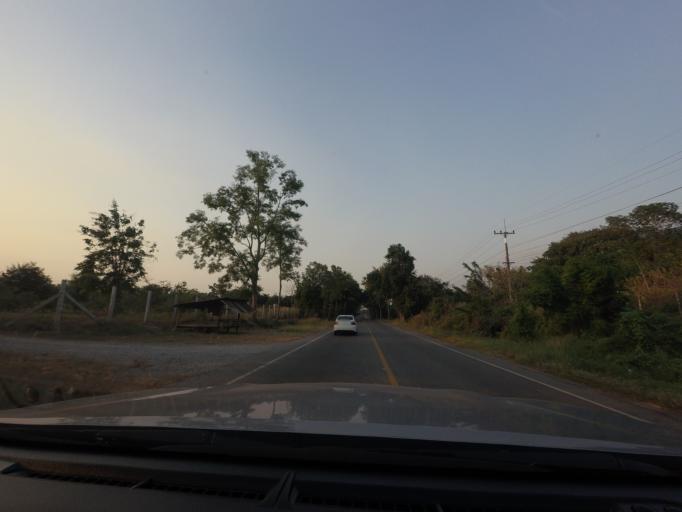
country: TH
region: Phitsanulok
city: Wang Thong
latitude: 16.7216
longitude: 100.4617
